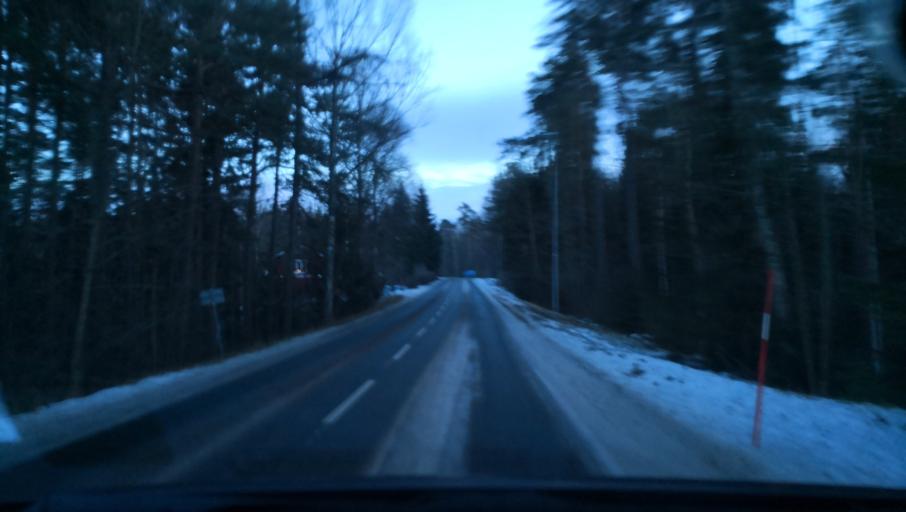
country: SE
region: Soedermanland
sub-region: Katrineholms Kommun
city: Katrineholm
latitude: 59.0843
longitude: 16.2202
